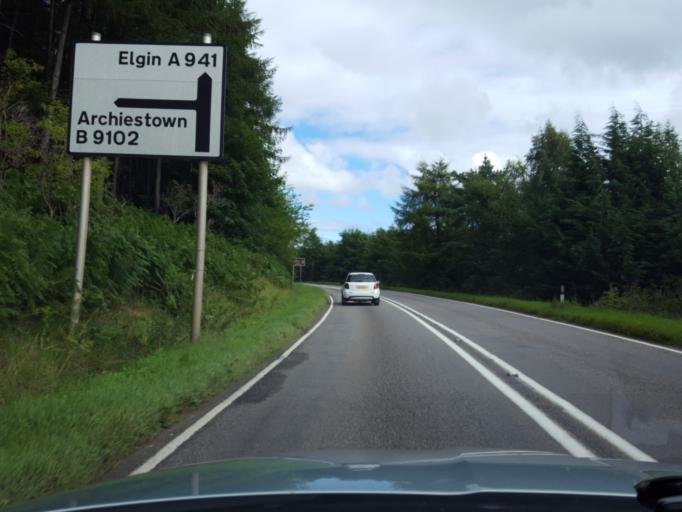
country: GB
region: Scotland
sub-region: Moray
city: Rothes
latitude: 57.4951
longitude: -3.1902
